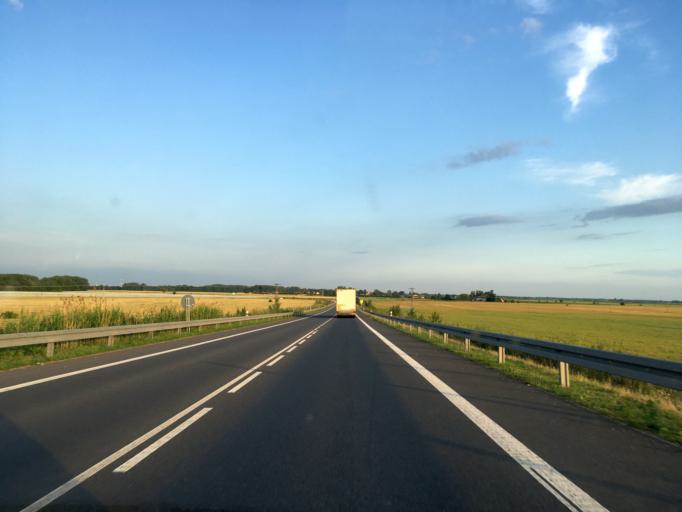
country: SK
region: Trnavsky
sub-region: Okres Galanta
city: Galanta
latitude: 48.1851
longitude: 17.7010
